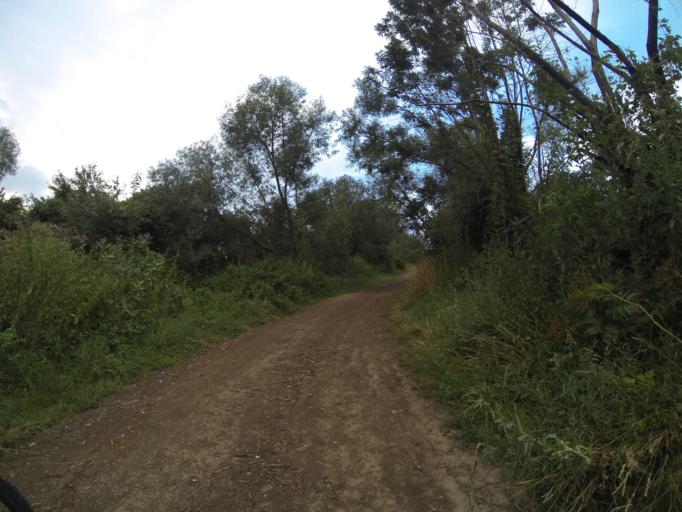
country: RO
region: Brasov
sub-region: Comuna Sinca Veche
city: Sinca Veche
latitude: 45.7619
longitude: 25.1759
